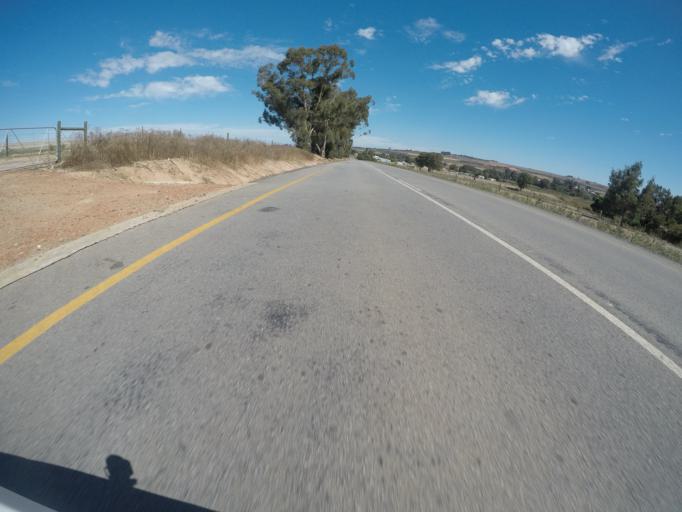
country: ZA
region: Western Cape
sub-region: West Coast District Municipality
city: Malmesbury
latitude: -33.4836
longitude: 18.6945
